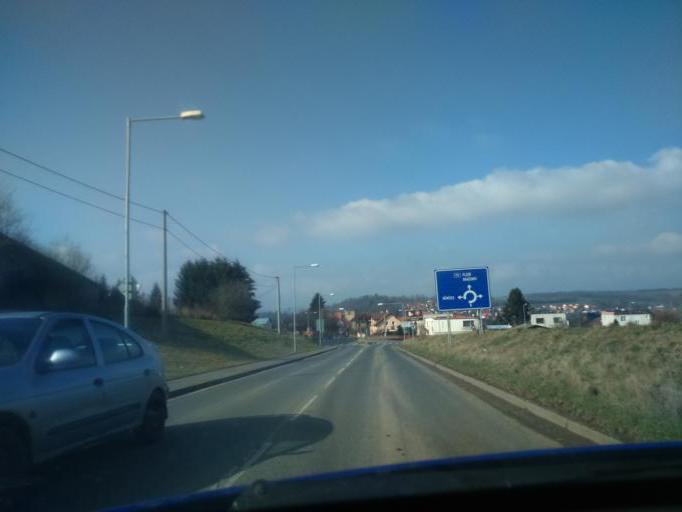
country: CZ
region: Plzensky
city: Horsovsky Tyn
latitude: 49.5212
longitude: 12.9476
